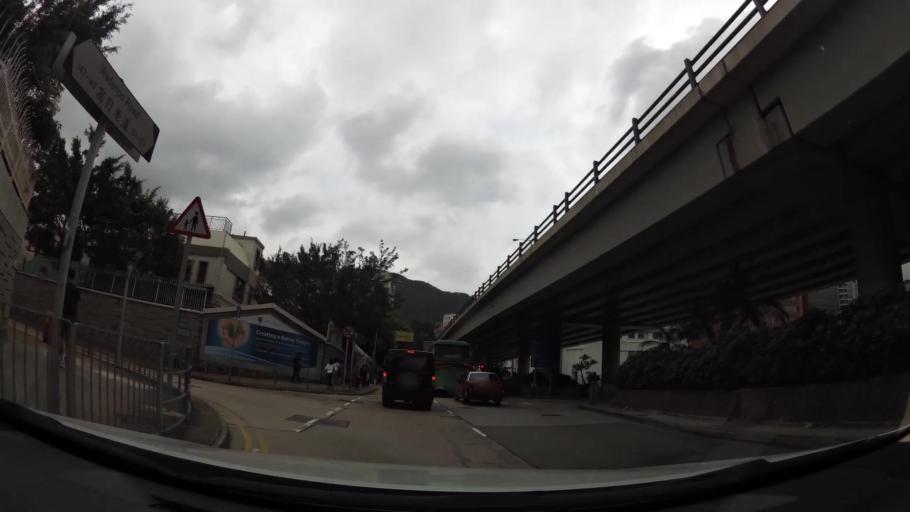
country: HK
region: Wong Tai Sin
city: Wong Tai Sin
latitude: 22.3385
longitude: 114.1789
